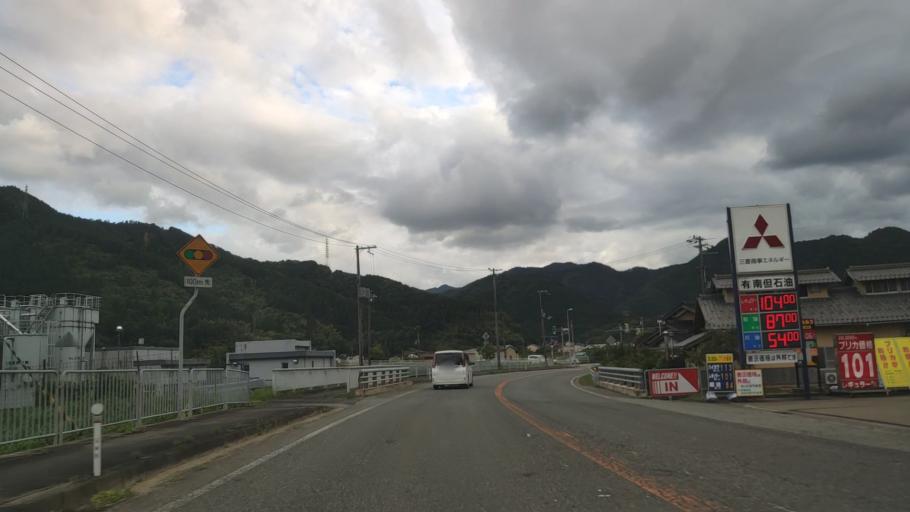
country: JP
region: Hyogo
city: Toyooka
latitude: 35.3853
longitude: 134.7870
